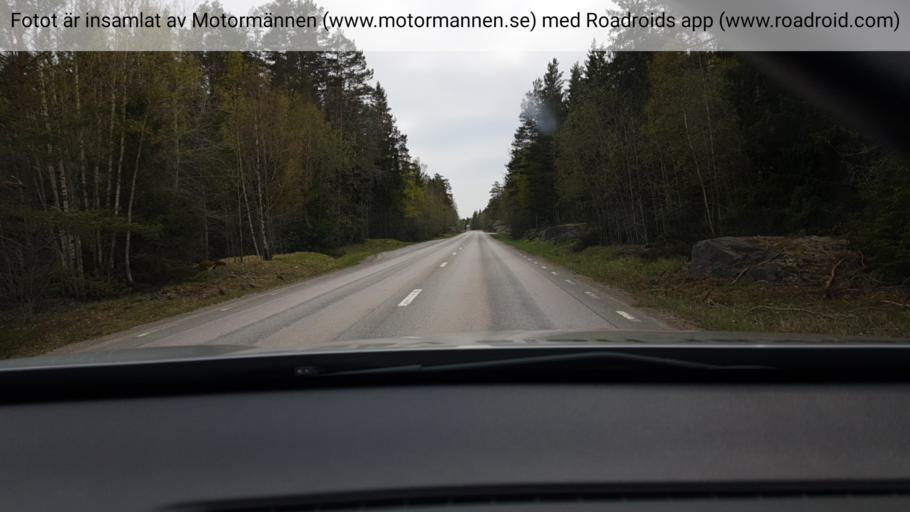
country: SE
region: Stockholm
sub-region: Norrtalje Kommun
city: Nykvarn
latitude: 59.9004
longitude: 18.0915
